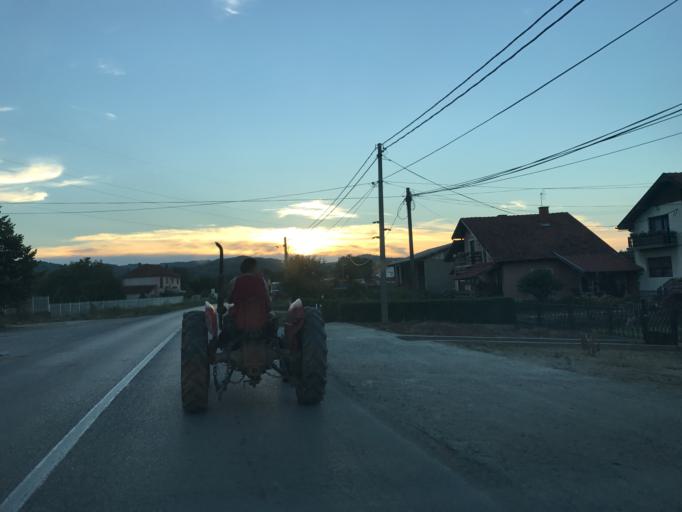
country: RS
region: Central Serbia
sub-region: Branicevski Okrug
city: Veliko Gradiste
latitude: 44.6999
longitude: 21.5350
